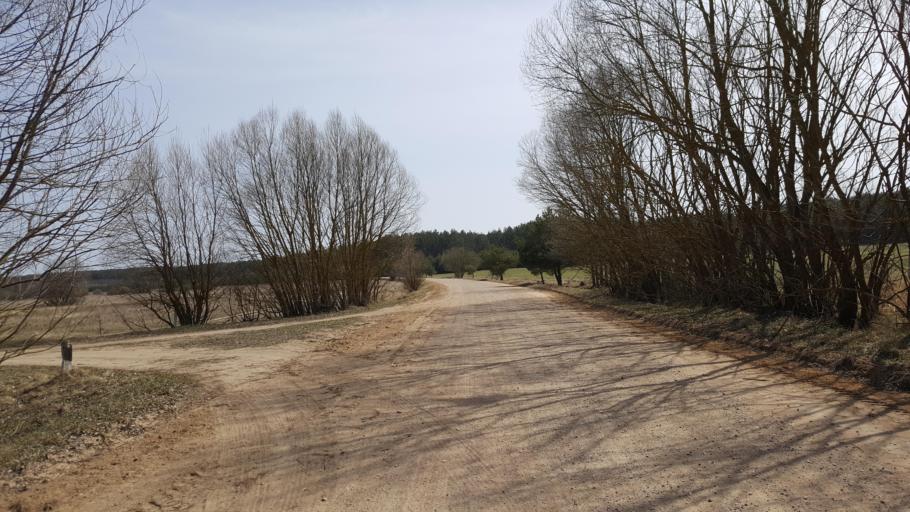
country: BY
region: Brest
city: Kamyanyuki
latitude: 52.5655
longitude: 23.7557
